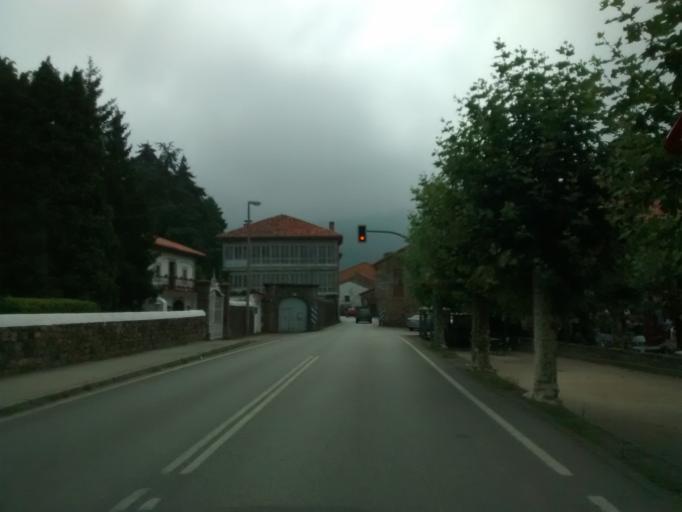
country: ES
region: Cantabria
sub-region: Provincia de Cantabria
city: Cabezon de la Sal
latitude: 43.2954
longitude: -4.2381
